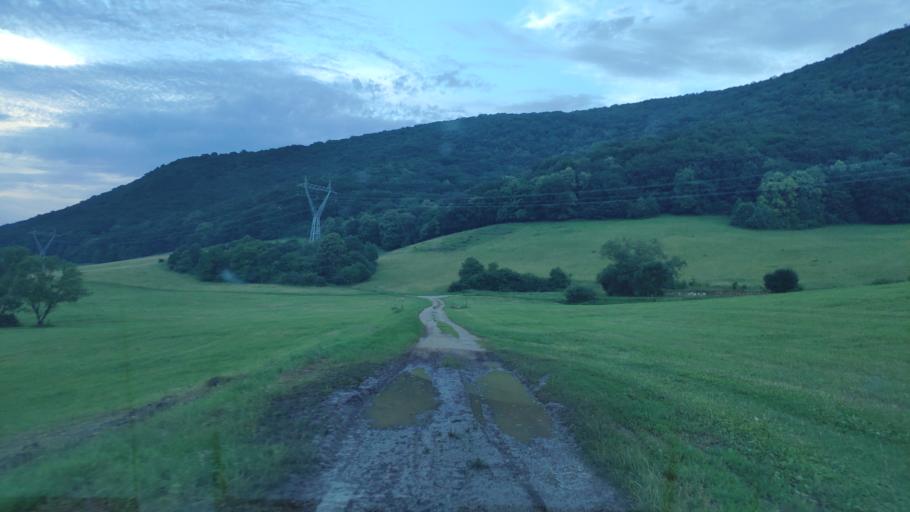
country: HU
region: Borsod-Abauj-Zemplen
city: Szendro
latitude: 48.5854
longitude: 20.7331
